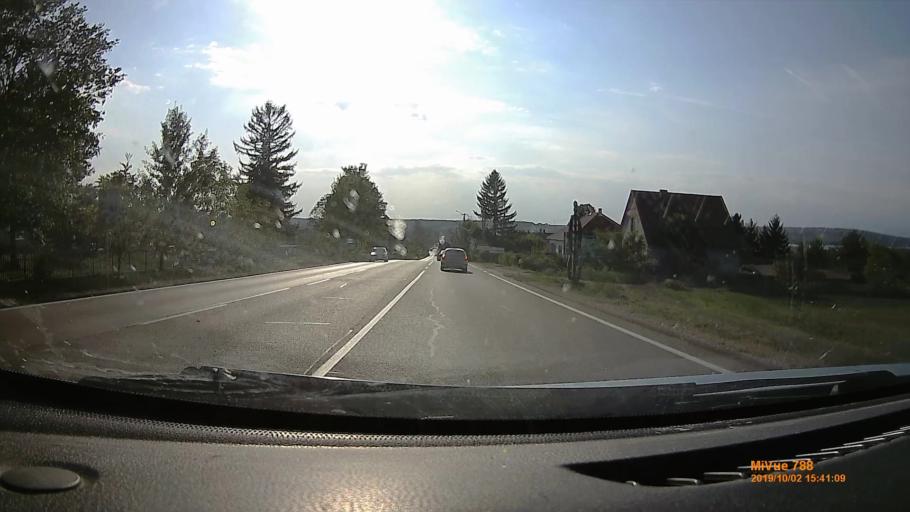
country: HU
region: Heves
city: Kerecsend
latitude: 47.7989
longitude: 20.3529
